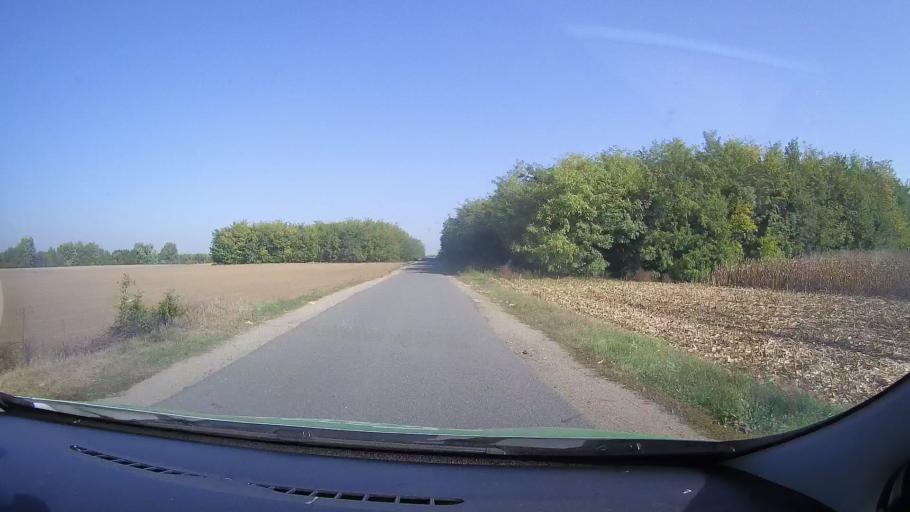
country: RO
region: Satu Mare
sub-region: Comuna Ciumesti
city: Ciumesti
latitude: 47.6884
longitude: 22.3537
